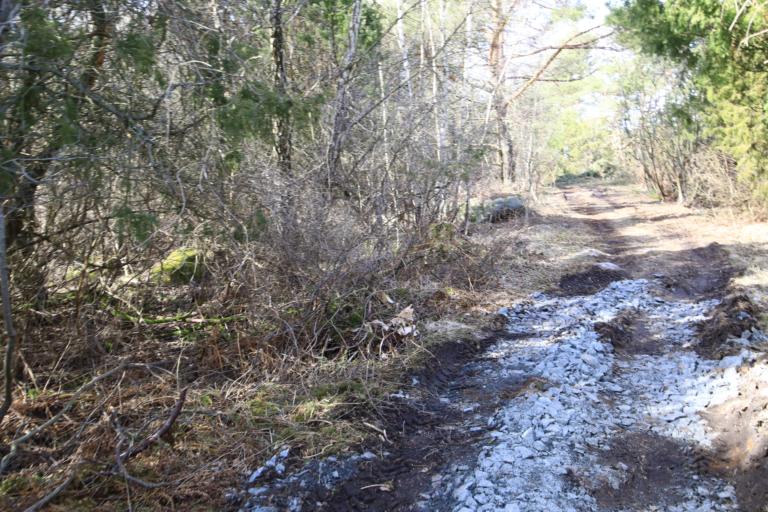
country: SE
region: Halland
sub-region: Kungsbacka Kommun
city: Frillesas
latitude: 57.2707
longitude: 12.1153
